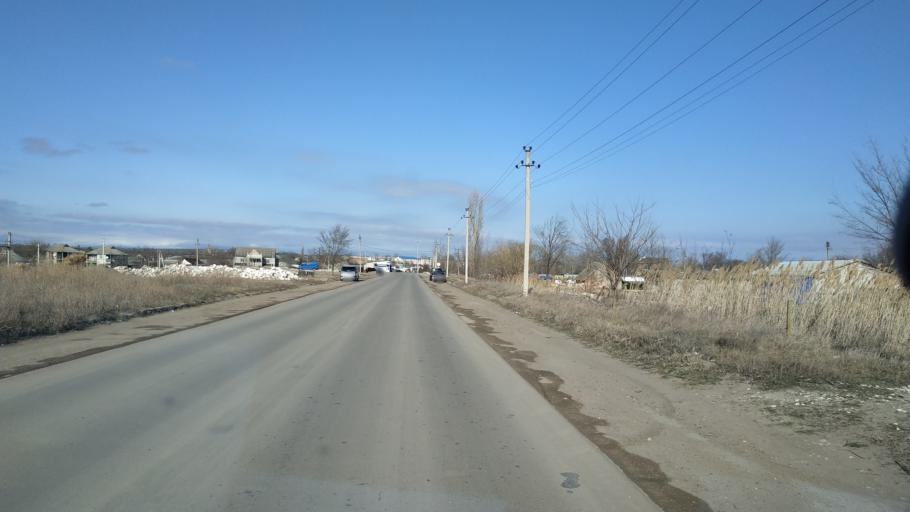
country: MD
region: Causeni
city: Causeni
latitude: 46.6458
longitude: 29.4053
